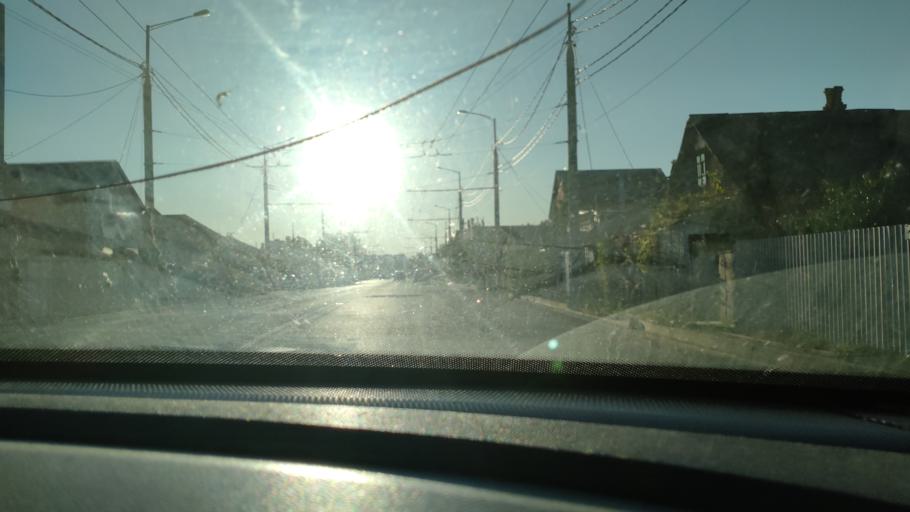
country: RU
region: Krasnodarskiy
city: Krasnodar
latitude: 45.0414
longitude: 38.9294
